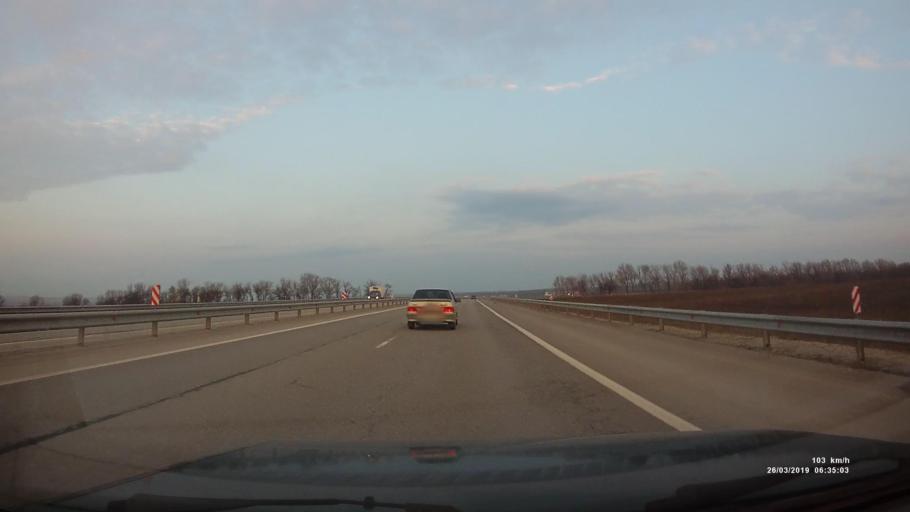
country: RU
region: Rostov
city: Chaltyr
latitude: 47.2786
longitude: 39.4541
